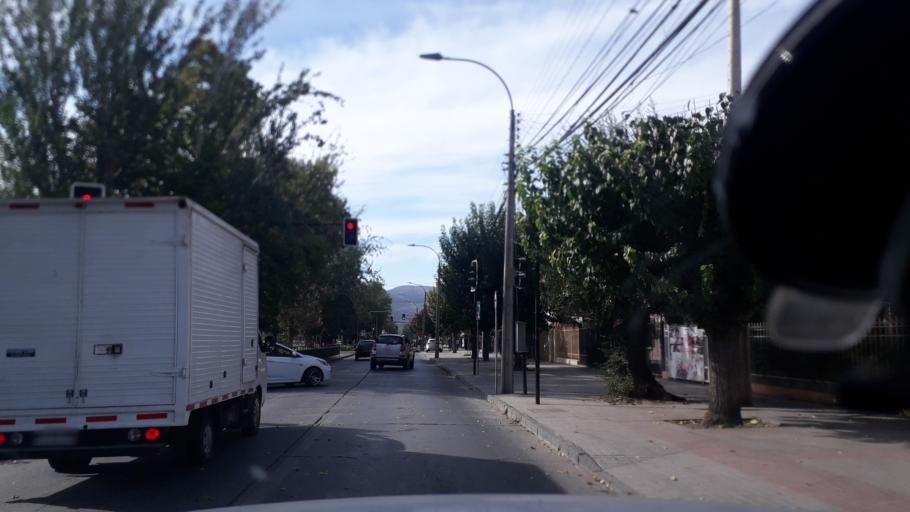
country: CL
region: Valparaiso
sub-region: Provincia de San Felipe
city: San Felipe
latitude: -32.7527
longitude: -70.7204
